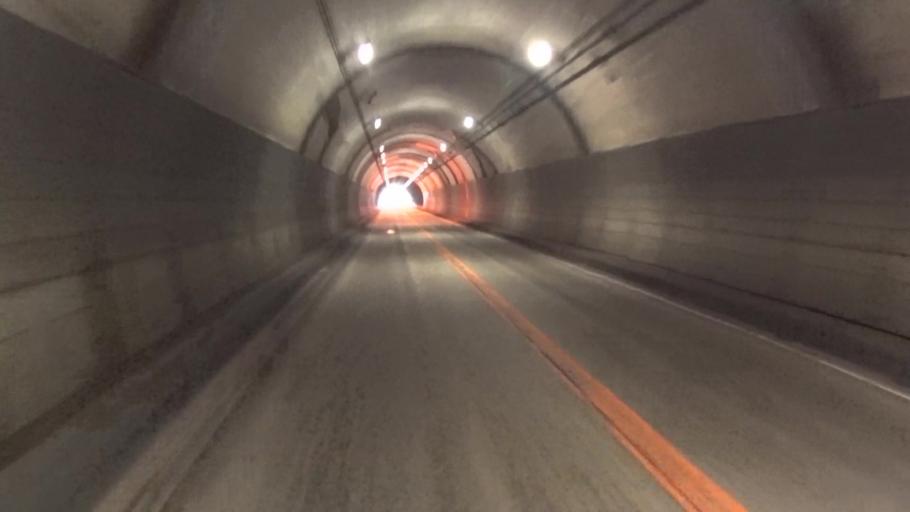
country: JP
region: Hyogo
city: Toyooka
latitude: 35.5840
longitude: 134.8627
